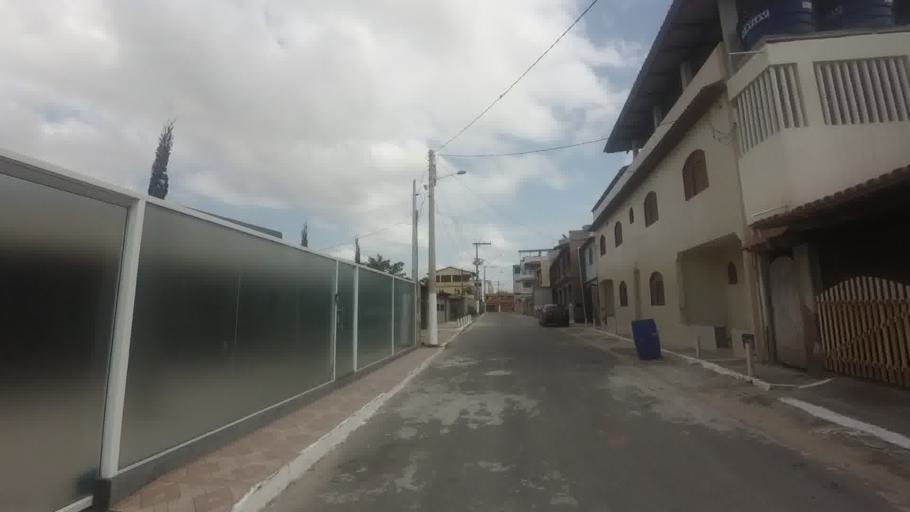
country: BR
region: Espirito Santo
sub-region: Piuma
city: Piuma
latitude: -20.8956
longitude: -40.7753
